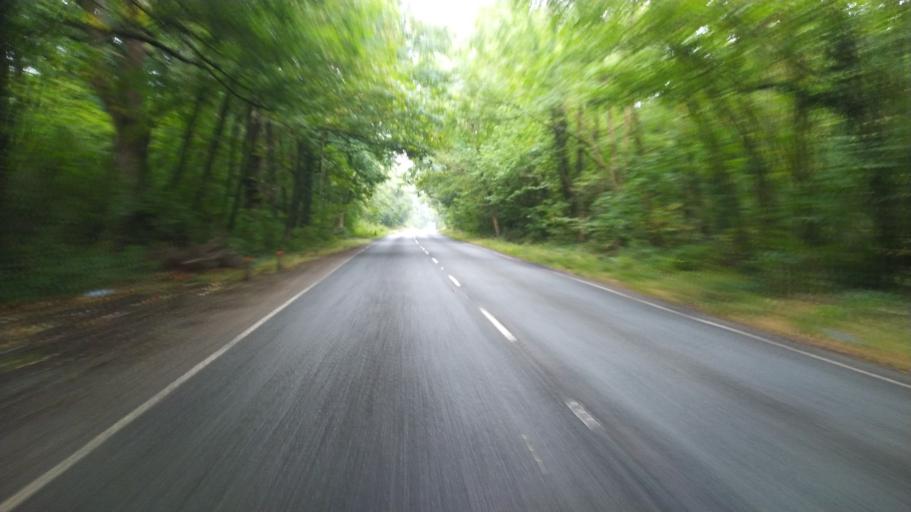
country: GB
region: England
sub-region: Hampshire
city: New Milton
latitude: 50.7825
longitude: -1.6944
